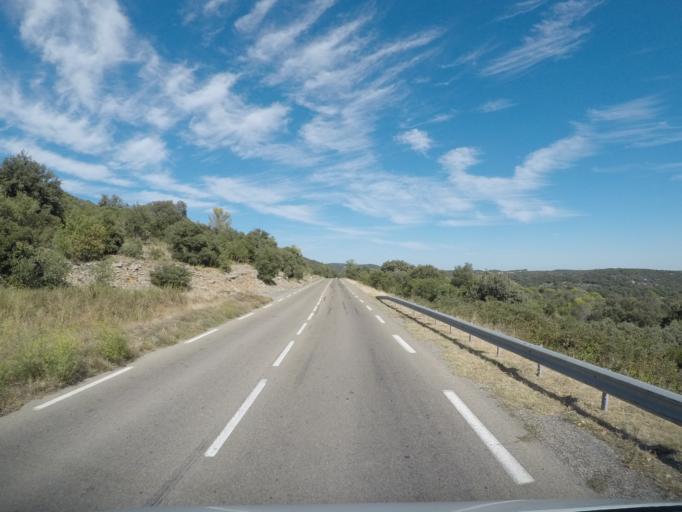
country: FR
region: Languedoc-Roussillon
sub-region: Departement du Gard
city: Sauve
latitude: 43.9608
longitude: 3.9091
